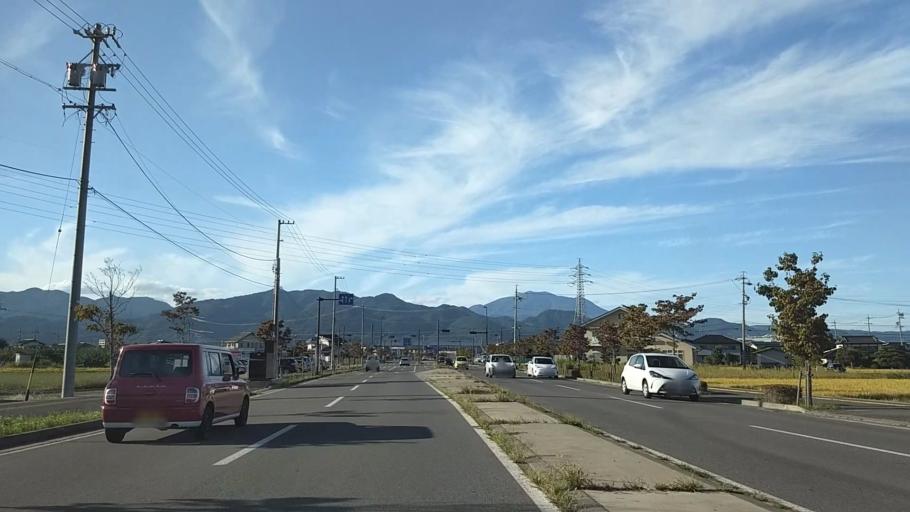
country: JP
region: Nagano
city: Nagano-shi
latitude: 36.5994
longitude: 138.1809
